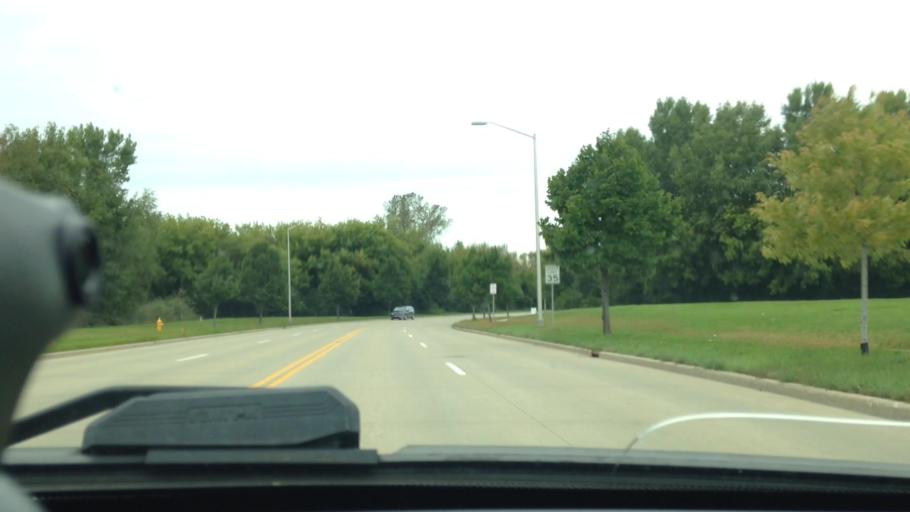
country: US
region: Wisconsin
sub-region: Fond du Lac County
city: North Fond du Lac
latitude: 43.7942
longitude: -88.4762
